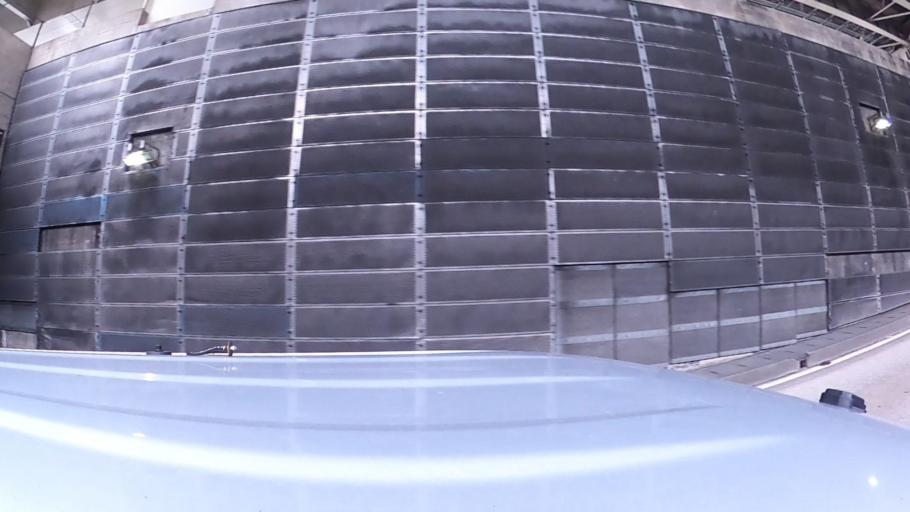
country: JP
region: Kanagawa
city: Yokohama
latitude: 35.4608
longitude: 139.6250
